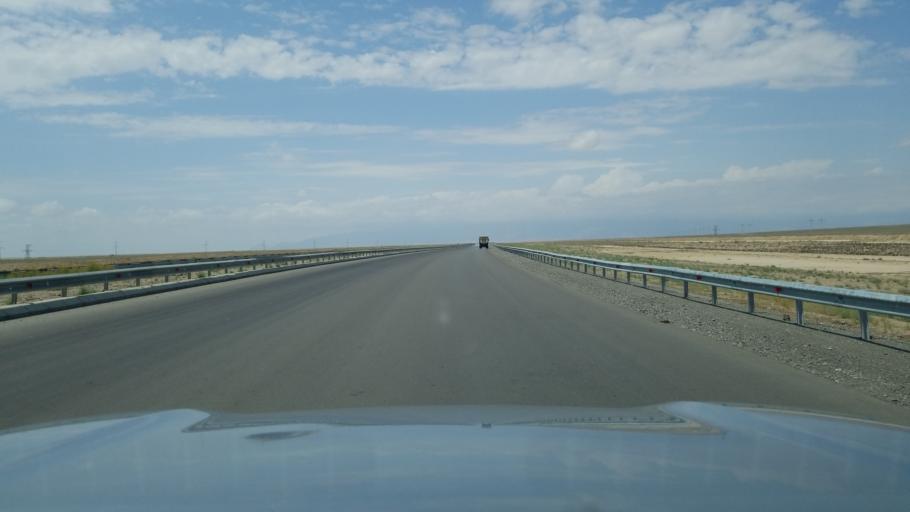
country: TM
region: Balkan
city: Gumdag
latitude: 39.2203
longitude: 54.7594
